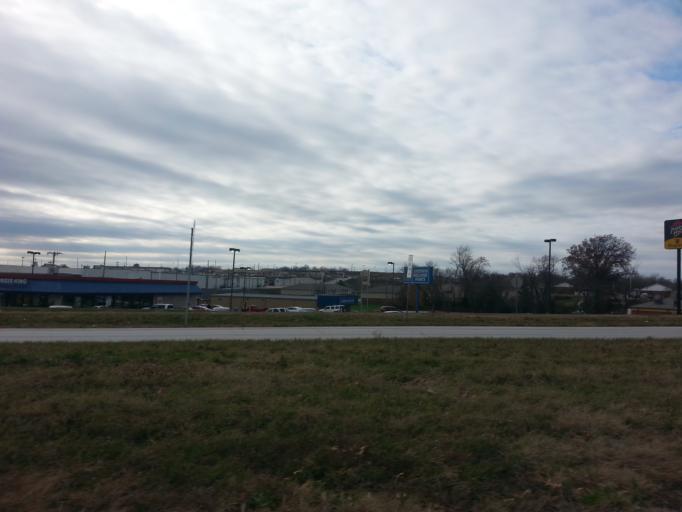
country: US
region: Missouri
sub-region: Marion County
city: Hannibal
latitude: 39.7264
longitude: -91.3921
